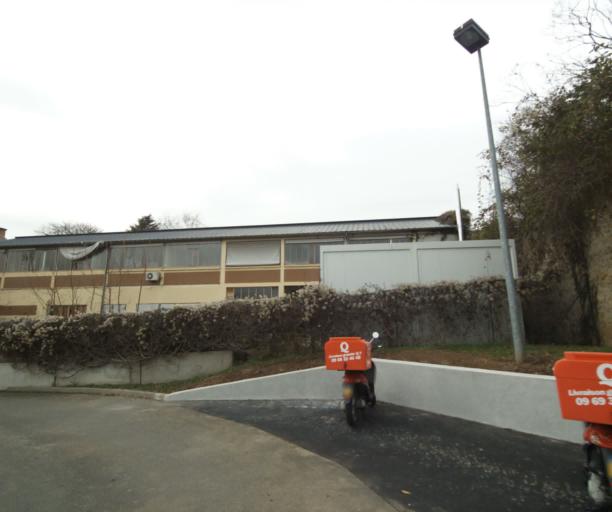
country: FR
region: Pays de la Loire
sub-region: Departement de la Sarthe
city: Le Mans
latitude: 47.9977
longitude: 0.2221
